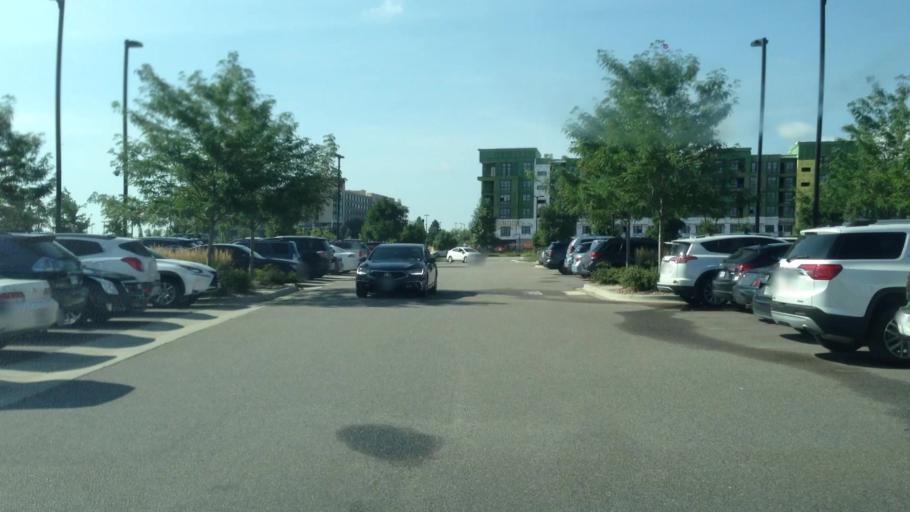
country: US
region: Colorado
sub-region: Douglas County
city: Meridian
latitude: 39.5449
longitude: -104.8720
